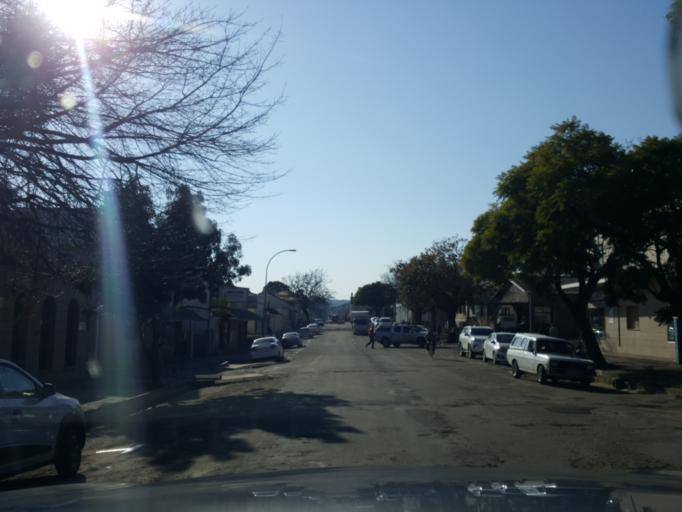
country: ZA
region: Eastern Cape
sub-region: Cacadu District Municipality
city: Grahamstown
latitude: -33.3097
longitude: 26.5239
